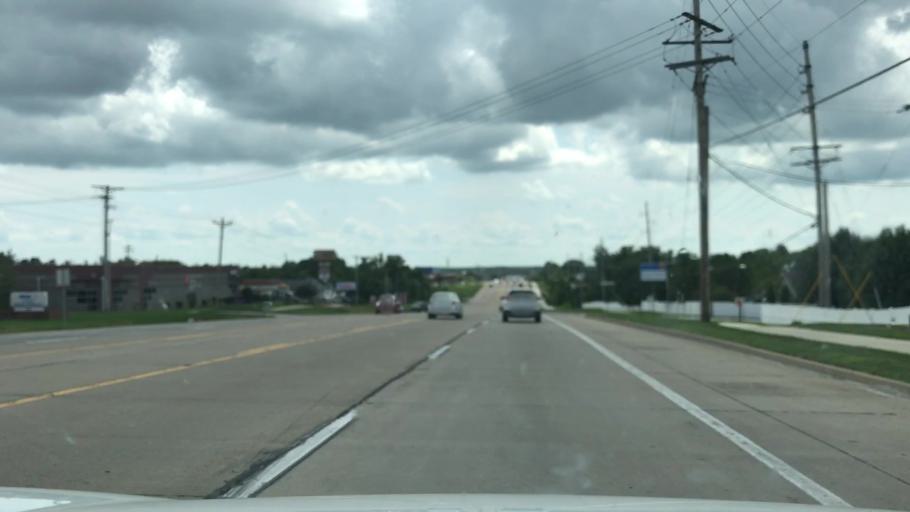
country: US
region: Missouri
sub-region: Saint Charles County
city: Dardenne Prairie
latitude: 38.7688
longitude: -90.7002
